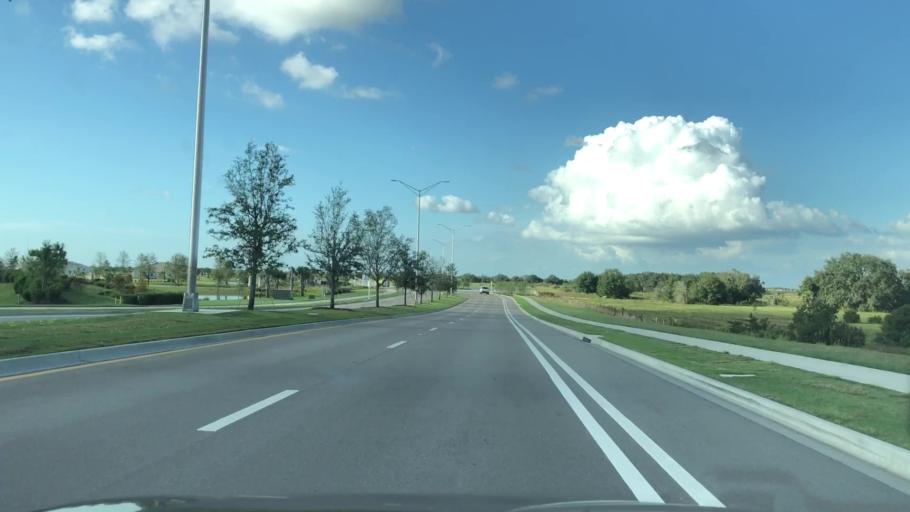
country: US
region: Florida
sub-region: Sarasota County
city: Fruitville
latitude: 27.3627
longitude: -82.3893
